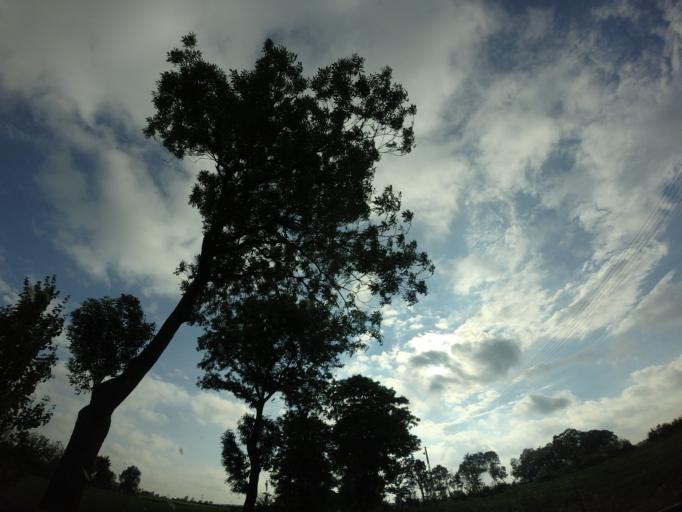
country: PL
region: Lodz Voivodeship
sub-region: Powiat kutnowski
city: Lanieta
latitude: 52.3605
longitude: 19.2593
